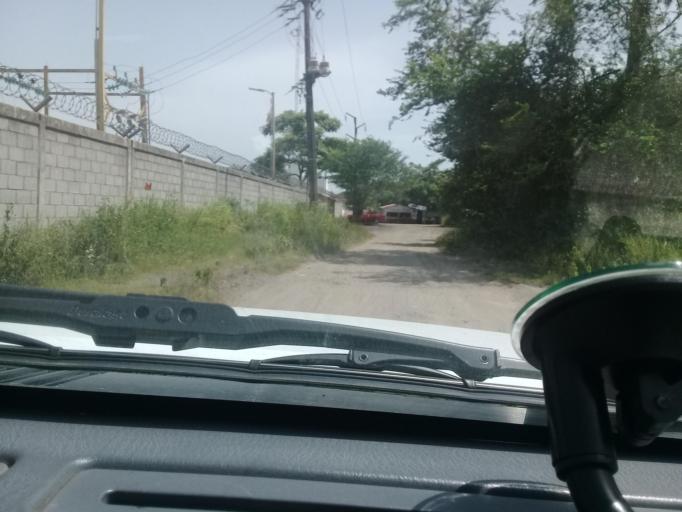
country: MX
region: Veracruz
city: Anahuac
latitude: 22.2282
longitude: -97.8327
